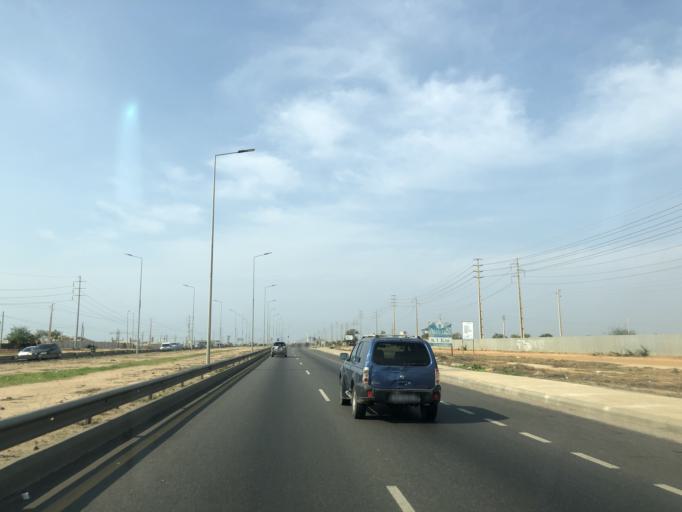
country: AO
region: Luanda
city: Luanda
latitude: -8.9613
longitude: 13.2569
